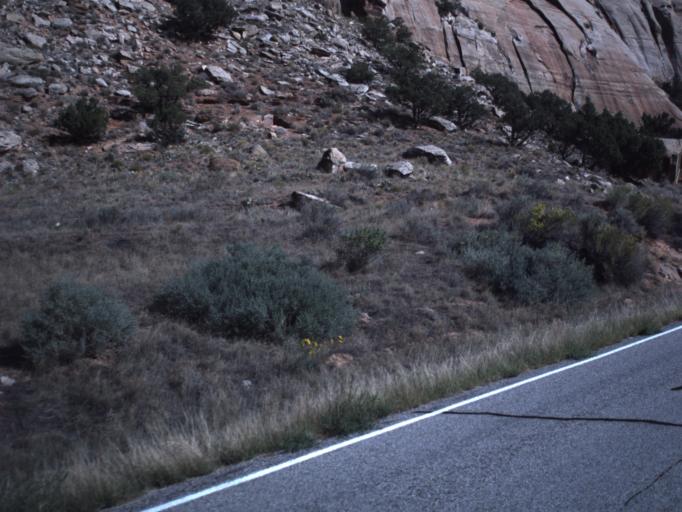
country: US
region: Utah
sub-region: San Juan County
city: Monticello
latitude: 38.0323
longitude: -109.5419
